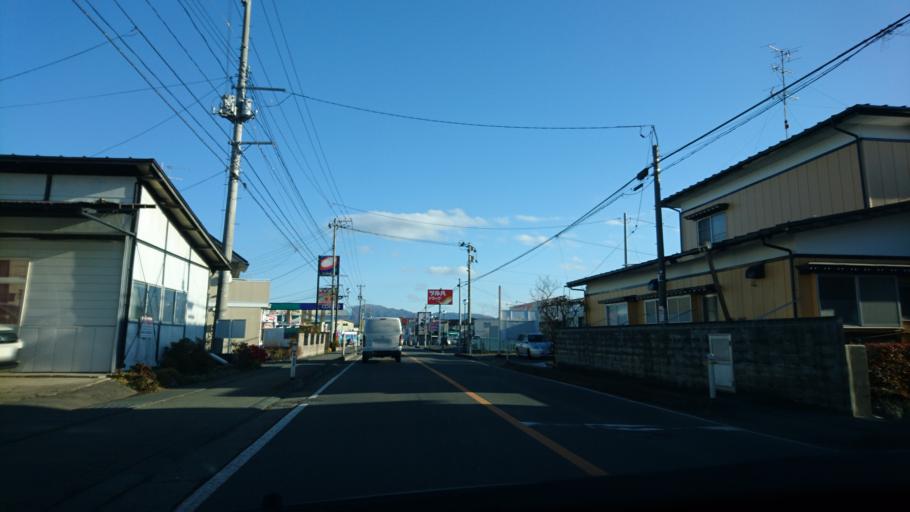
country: JP
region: Iwate
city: Mizusawa
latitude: 39.1315
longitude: 141.1529
